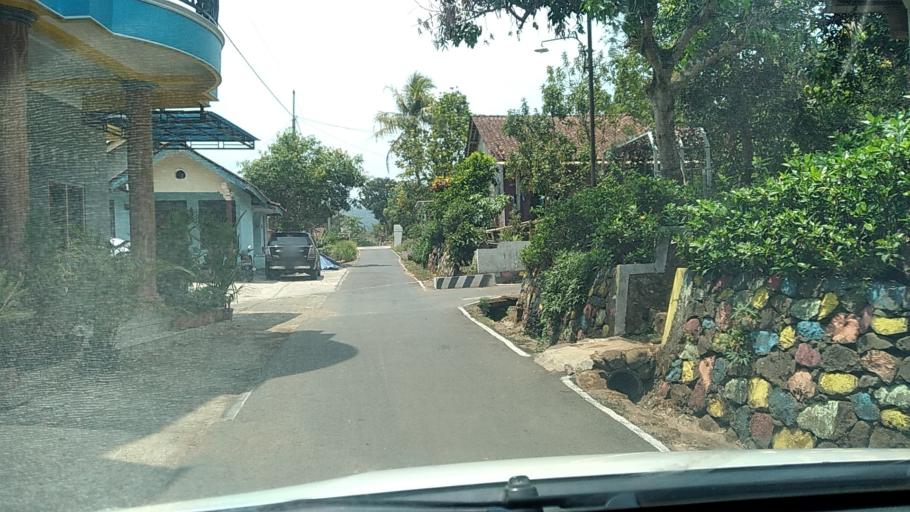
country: ID
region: Central Java
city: Ungaran
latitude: -7.0989
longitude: 110.3447
